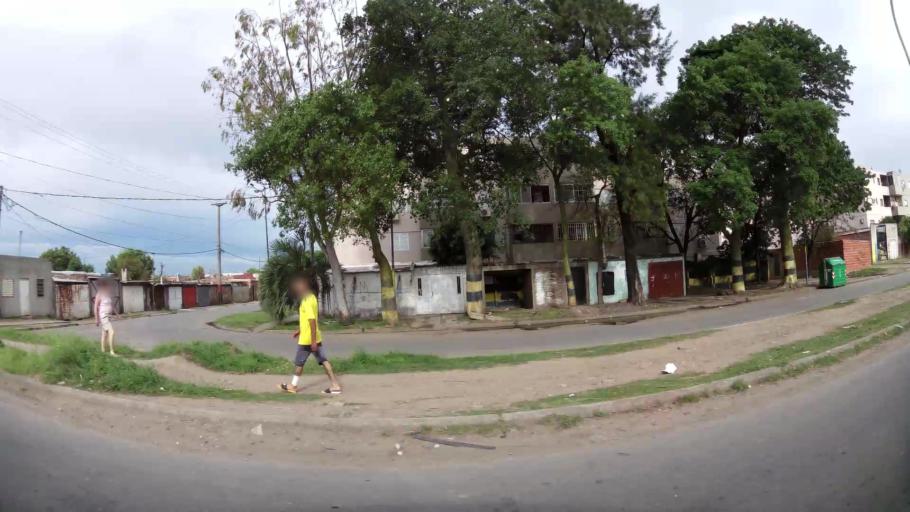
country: AR
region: Santa Fe
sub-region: Departamento de Rosario
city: Rosario
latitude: -32.9828
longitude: -60.6886
